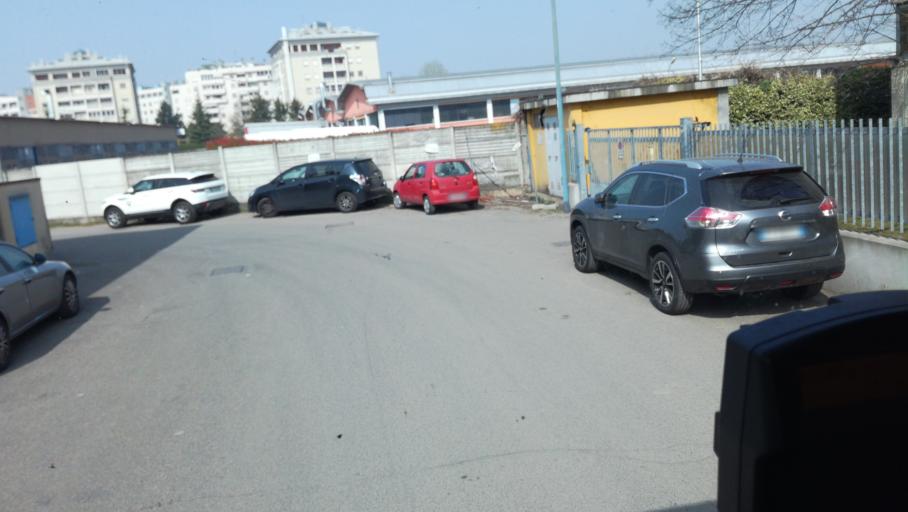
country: IT
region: Lombardy
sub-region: Citta metropolitana di Milano
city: Fizzonasco
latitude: 45.3750
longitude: 9.1822
